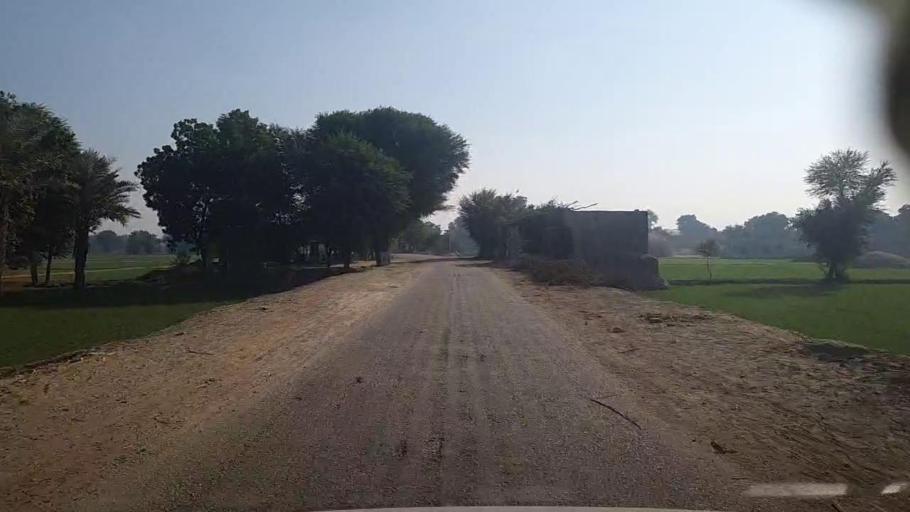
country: PK
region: Sindh
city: Kandiari
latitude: 26.8166
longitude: 68.4952
